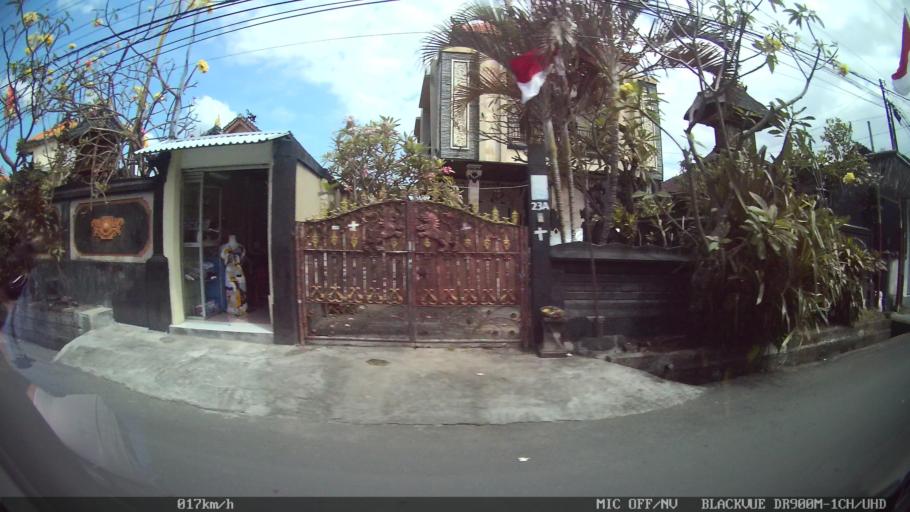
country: ID
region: Bali
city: Karyadharma
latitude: -8.6792
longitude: 115.1844
